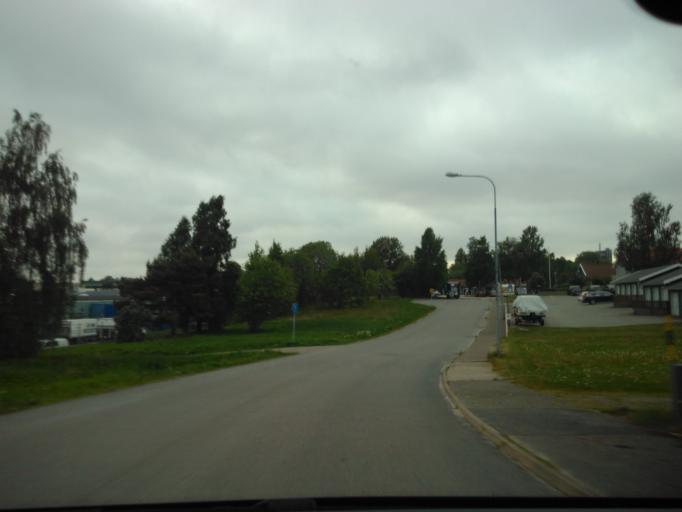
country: SE
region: Vaestra Goetaland
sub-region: Vargarda Kommun
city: Vargarda
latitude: 58.0255
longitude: 12.7967
